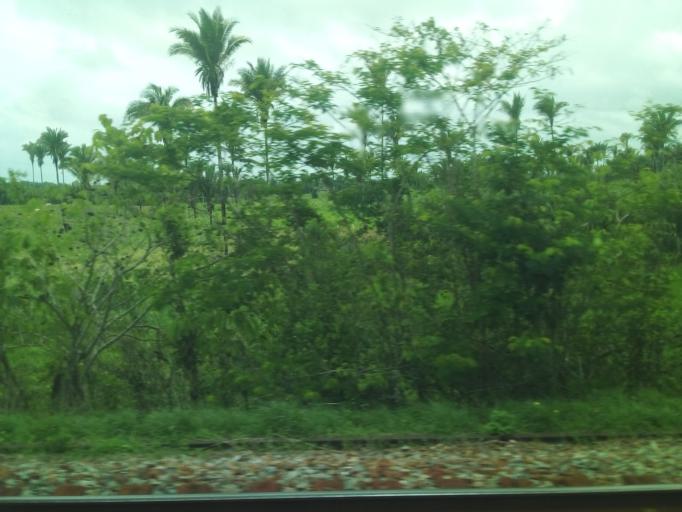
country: BR
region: Maranhao
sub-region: Vitoria Do Mearim
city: Vitoria do Mearim
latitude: -3.5371
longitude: -44.8834
